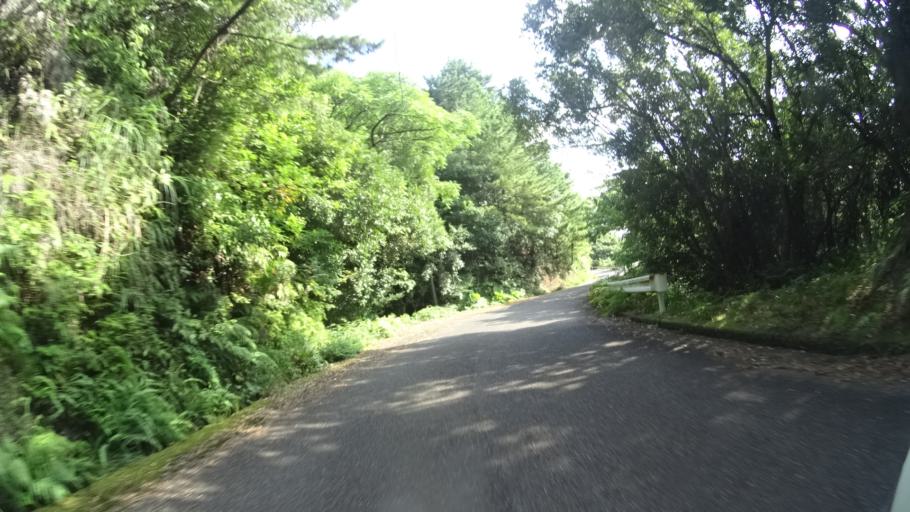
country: JP
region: Kagoshima
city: Nishinoomote
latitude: 30.3851
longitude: 130.3817
